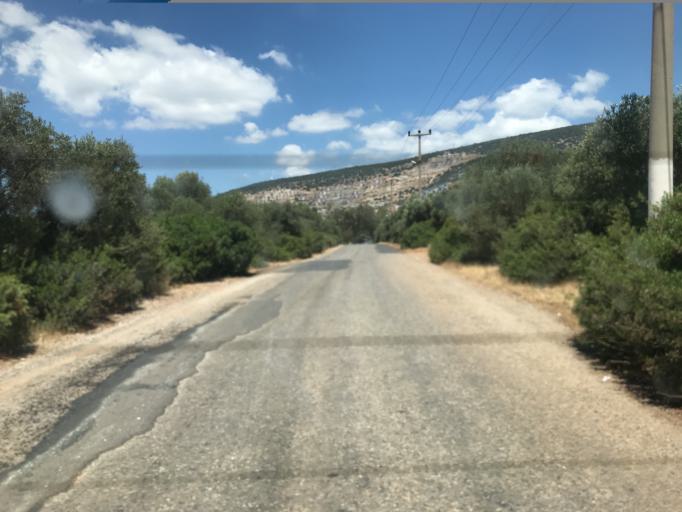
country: TR
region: Aydin
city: Sarikemer
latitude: 37.4114
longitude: 27.4229
